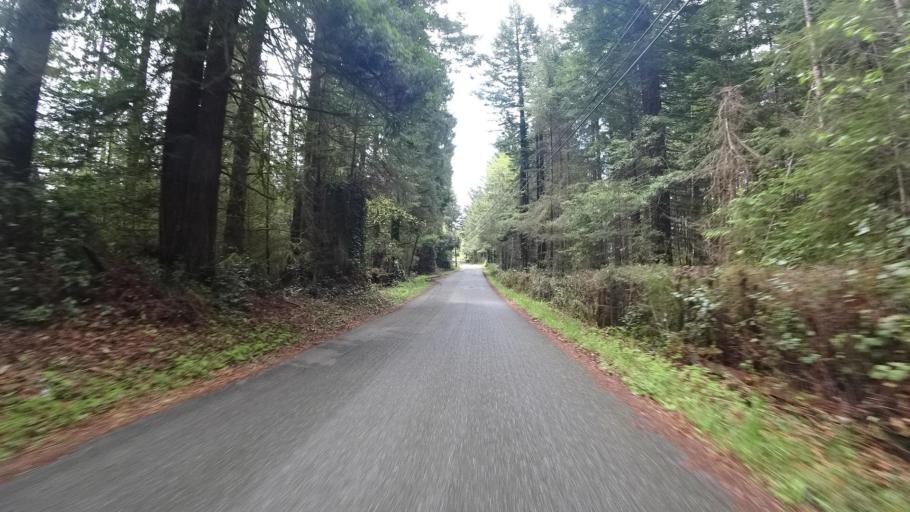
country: US
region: California
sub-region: Humboldt County
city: Bayside
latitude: 40.8530
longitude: -124.0315
